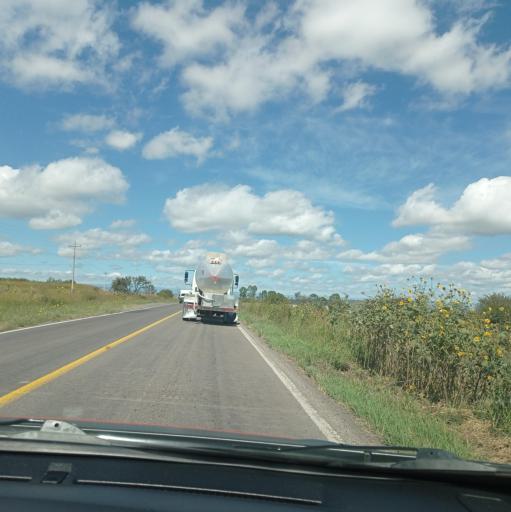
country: MX
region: Jalisco
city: Valle de Guadalupe
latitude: 21.0294
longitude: -102.5516
